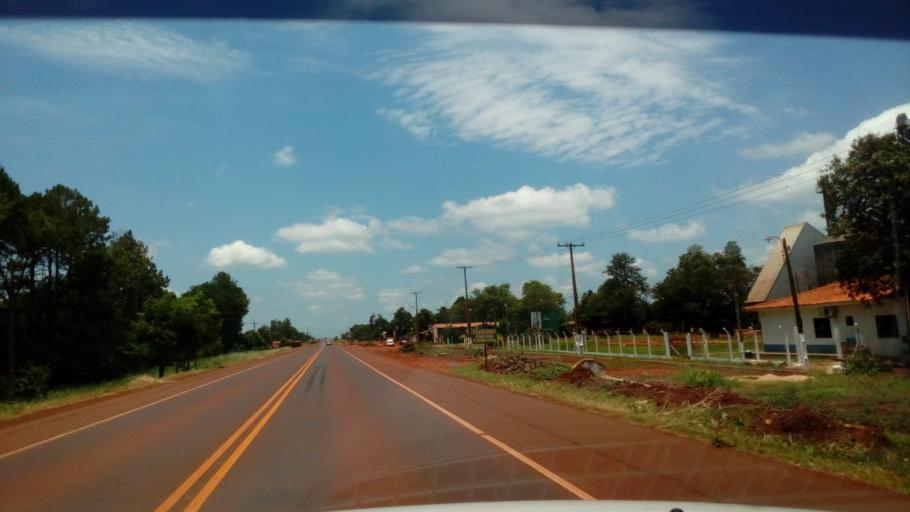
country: PY
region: Alto Parana
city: Naranjal
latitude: -26.0173
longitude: -55.1257
